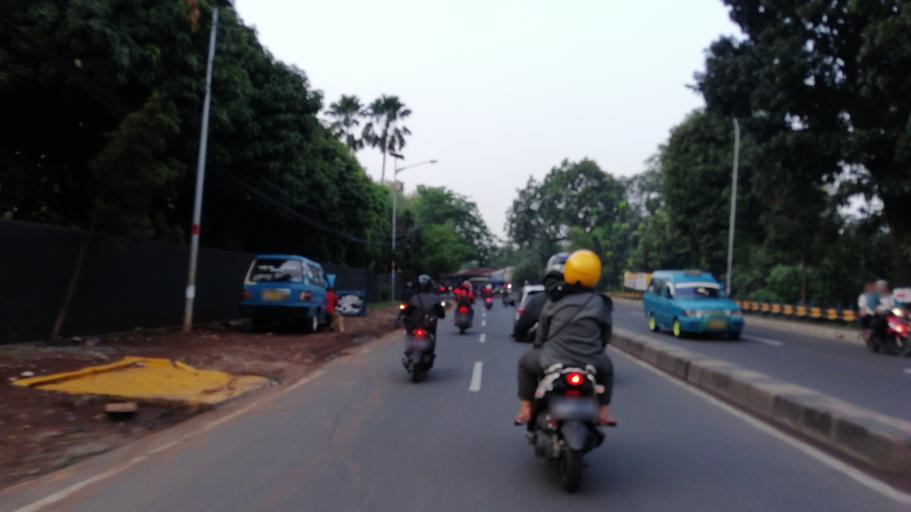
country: ID
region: West Java
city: Depok
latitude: -6.4070
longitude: 106.8621
